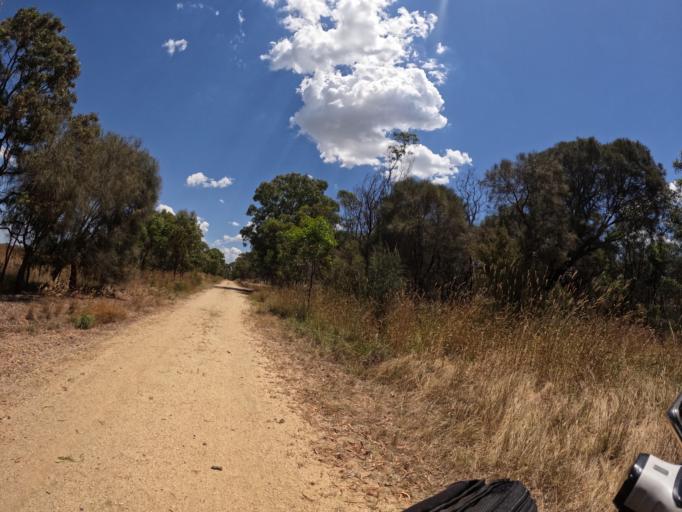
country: AU
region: Victoria
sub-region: Wellington
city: Heyfield
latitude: -37.9789
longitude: 146.8497
